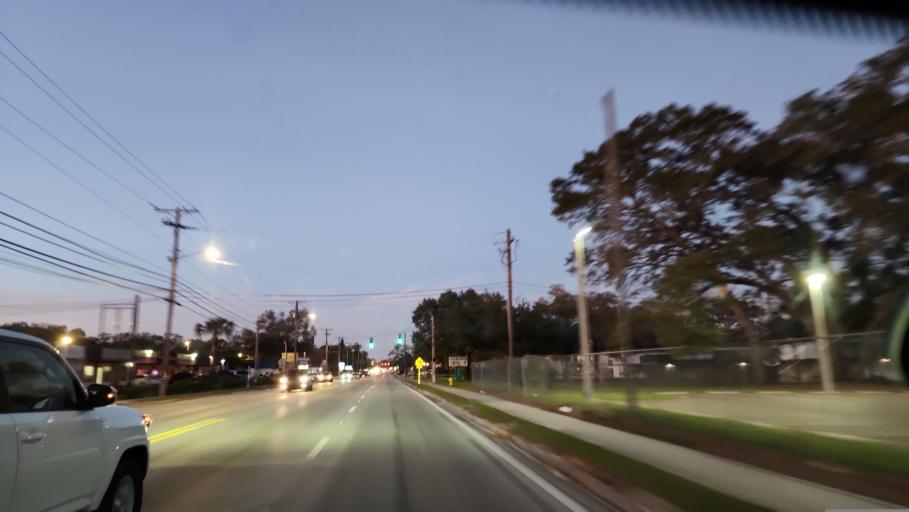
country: US
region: Florida
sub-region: Hillsborough County
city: Egypt Lake-Leto
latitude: 28.0038
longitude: -82.4843
